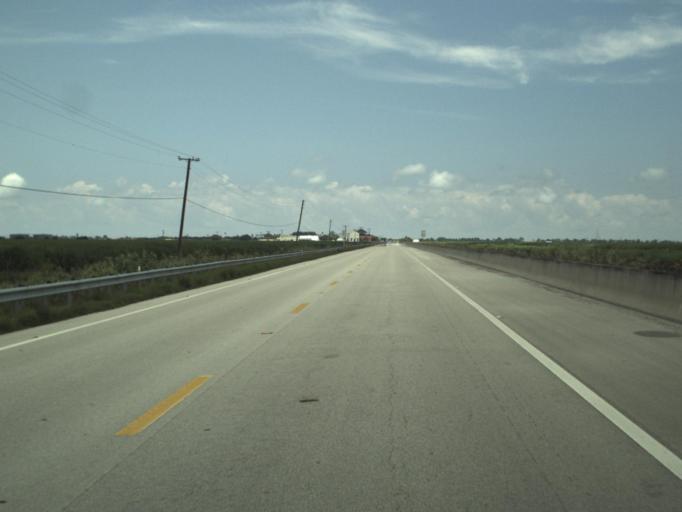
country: US
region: Florida
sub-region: Palm Beach County
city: Pahokee
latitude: 26.8381
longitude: -80.5967
